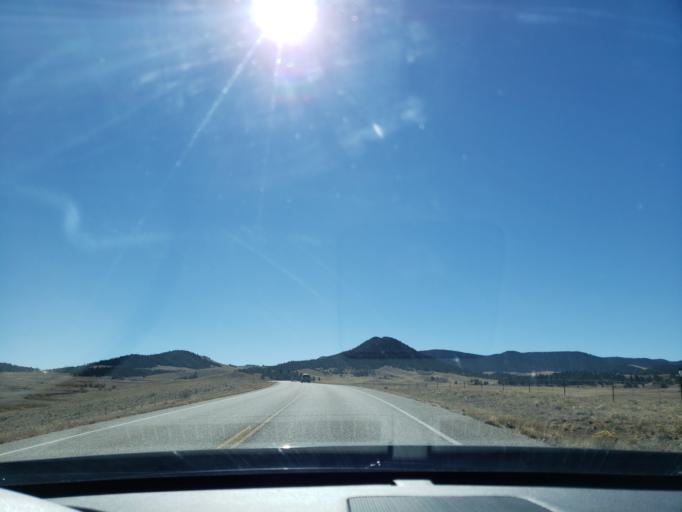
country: US
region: Colorado
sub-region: Chaffee County
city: Salida
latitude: 38.8557
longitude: -105.6535
